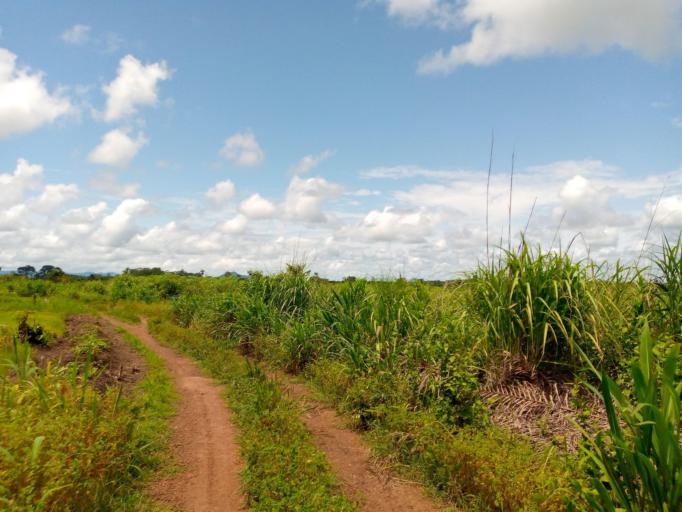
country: SL
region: Northern Province
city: Magburaka
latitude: 8.7176
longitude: -11.9224
